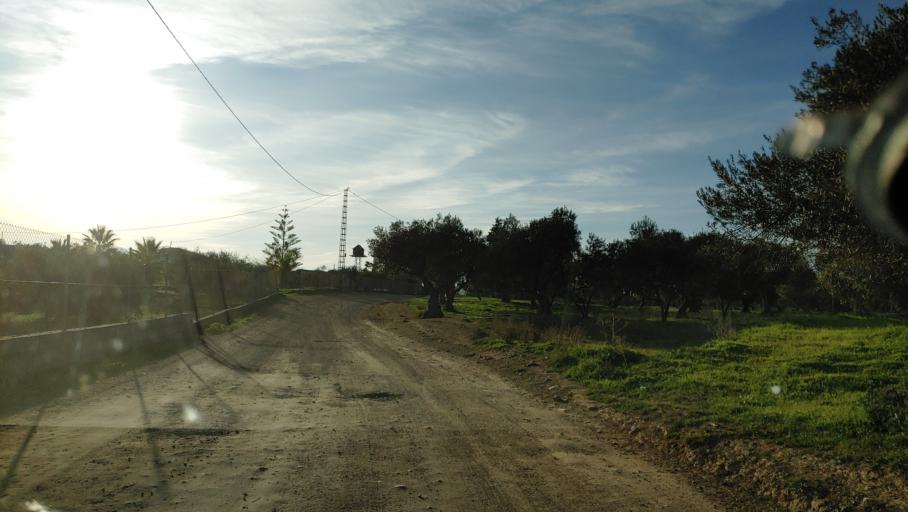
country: ES
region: Andalusia
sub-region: Provincia de Malaga
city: Cartama
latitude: 36.6823
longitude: -4.6403
